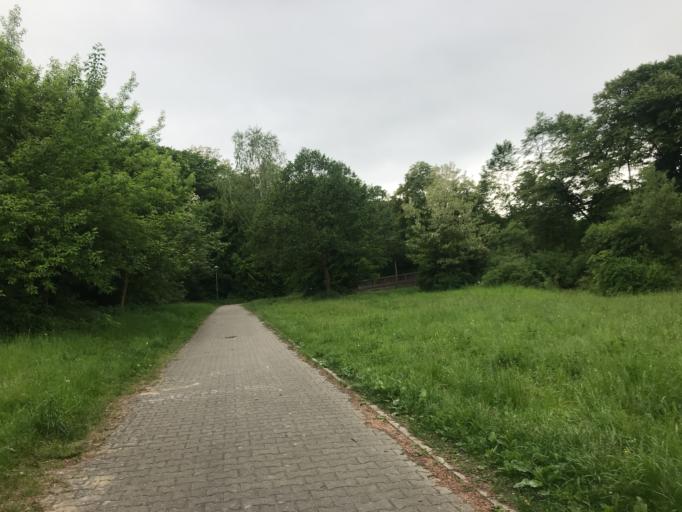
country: DE
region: Brandenburg
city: Melchow
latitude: 52.8448
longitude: 13.6969
